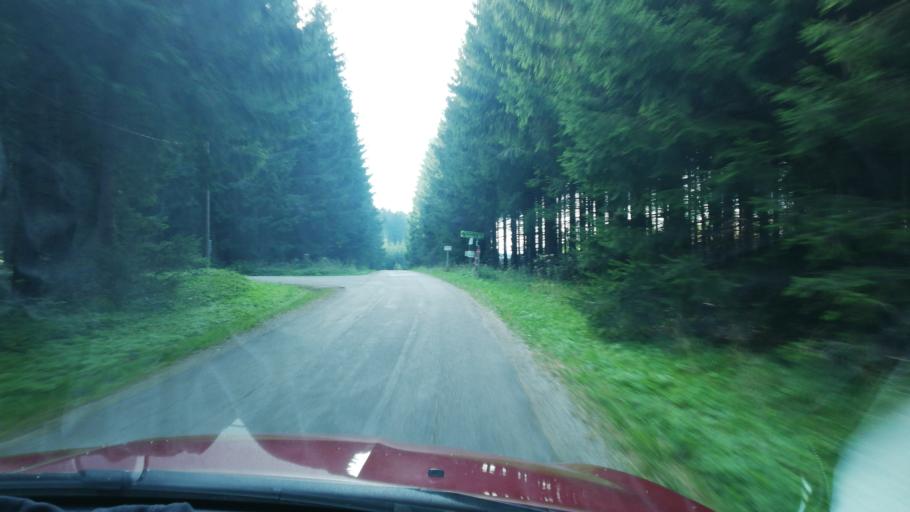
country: AT
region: Lower Austria
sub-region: Politischer Bezirk Zwettl
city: Langschlag
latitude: 48.4716
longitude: 14.8236
